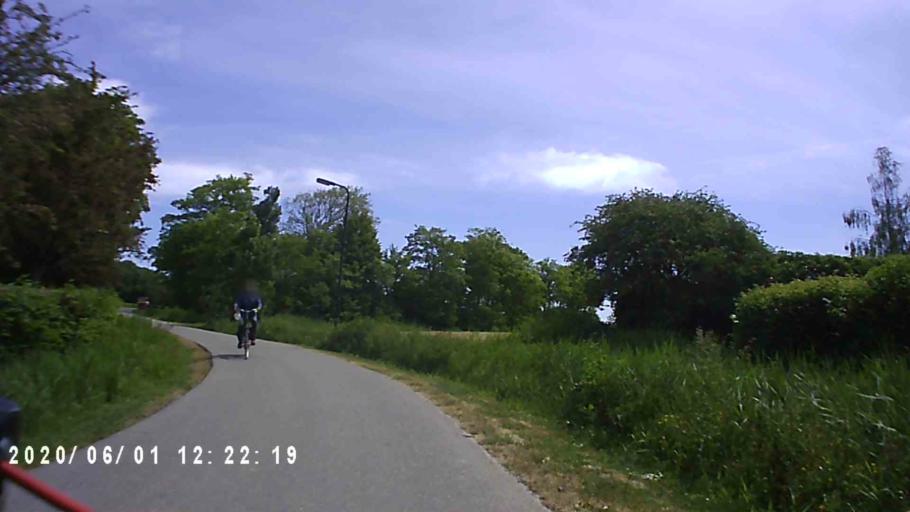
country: NL
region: Friesland
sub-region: Gemeente Harlingen
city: Harlingen
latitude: 53.1291
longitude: 5.4798
